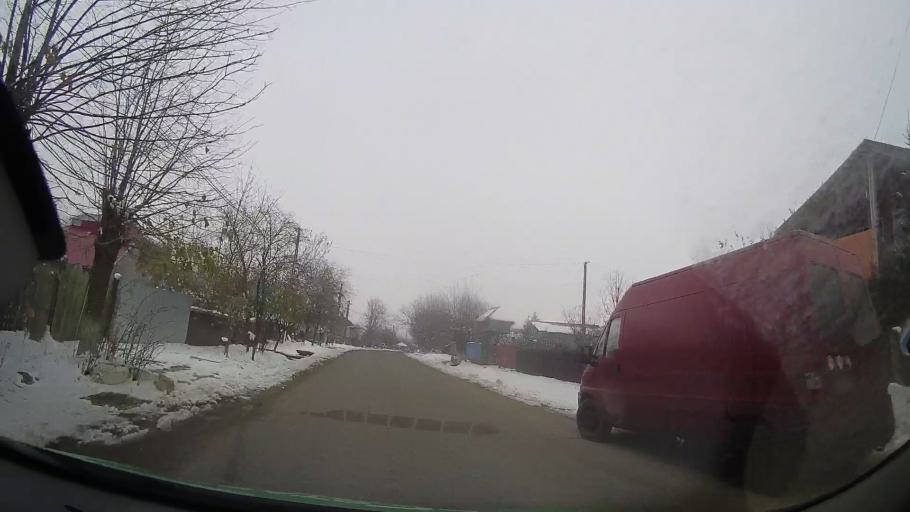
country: RO
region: Bacau
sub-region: Comuna Vultureni
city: Vultureni
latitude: 46.4032
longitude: 27.2732
